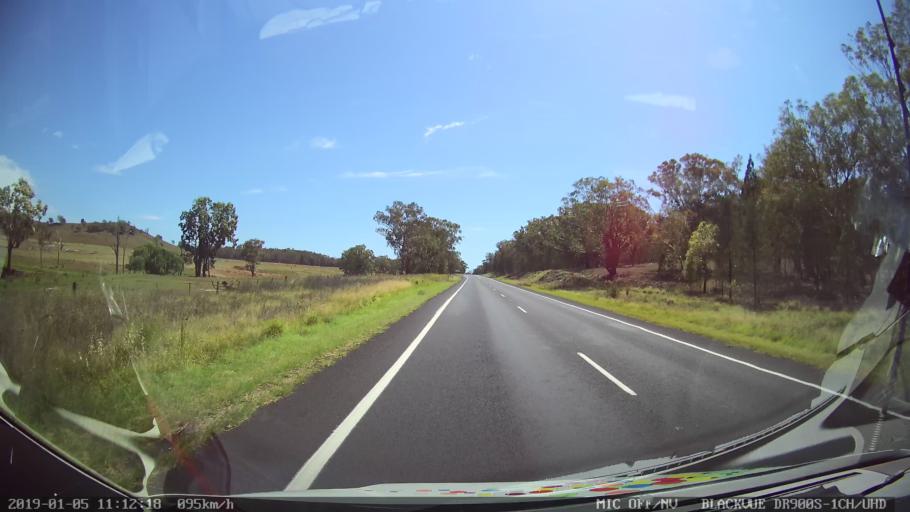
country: AU
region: New South Wales
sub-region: Warrumbungle Shire
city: Coonabarabran
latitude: -31.3834
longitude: 149.2593
